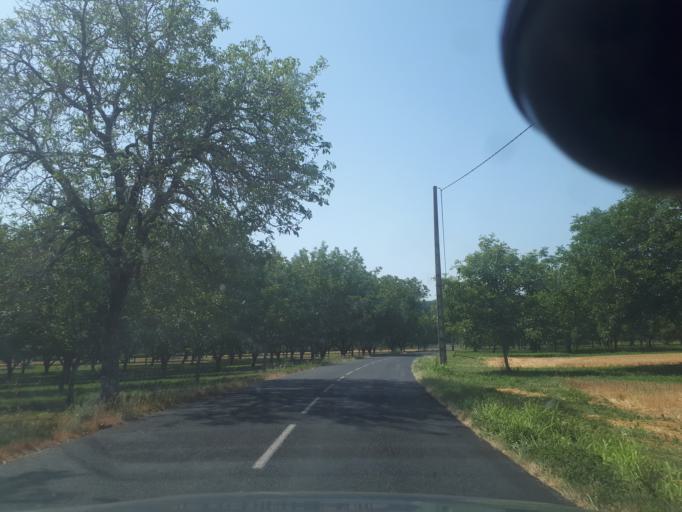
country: FR
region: Midi-Pyrenees
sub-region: Departement du Lot
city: Souillac
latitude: 44.8762
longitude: 1.4453
